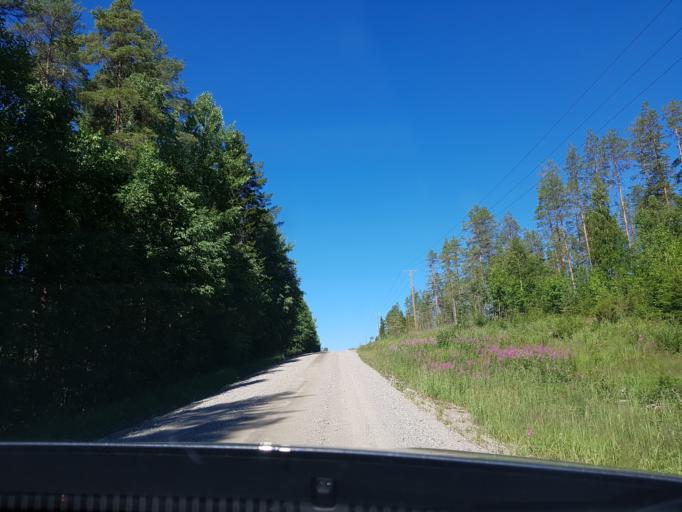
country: FI
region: Kainuu
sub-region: Kehys-Kainuu
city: Kuhmo
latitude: 64.1698
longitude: 29.6447
